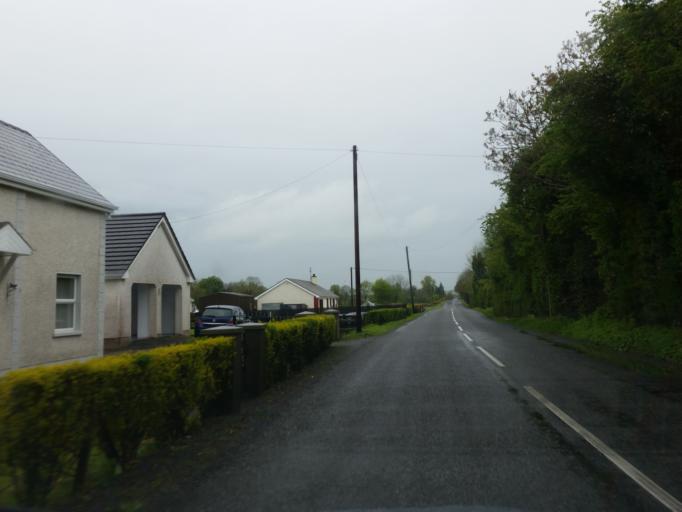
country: GB
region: Northern Ireland
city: Lisnaskea
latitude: 54.2184
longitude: -7.4639
